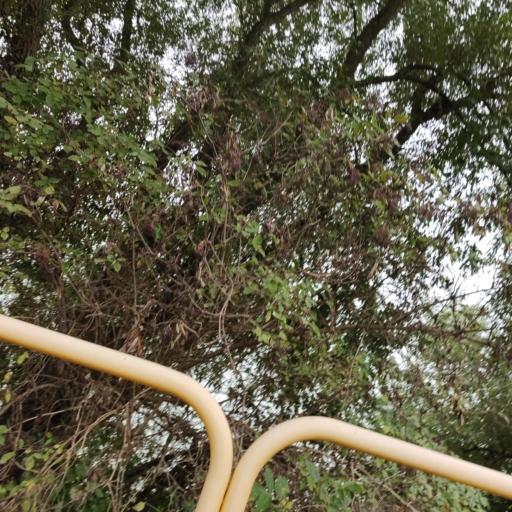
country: PL
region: Kujawsko-Pomorskie
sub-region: Powiat zninski
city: Znin
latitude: 52.8568
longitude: 17.7527
